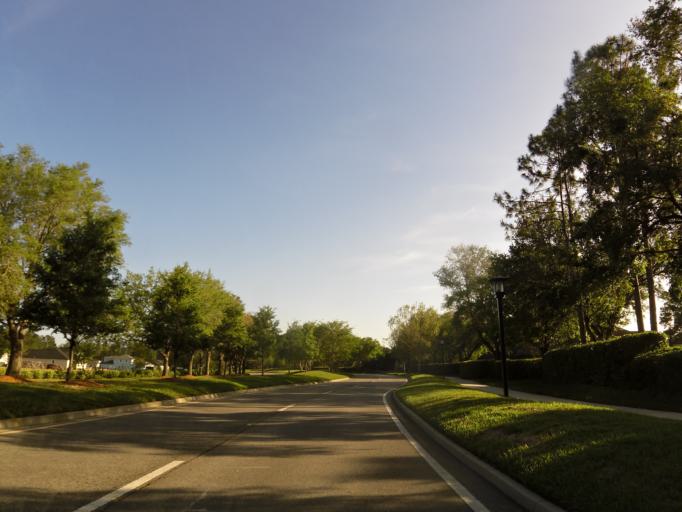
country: US
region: Florida
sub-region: Saint Johns County
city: Villano Beach
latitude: 29.9812
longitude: -81.4766
